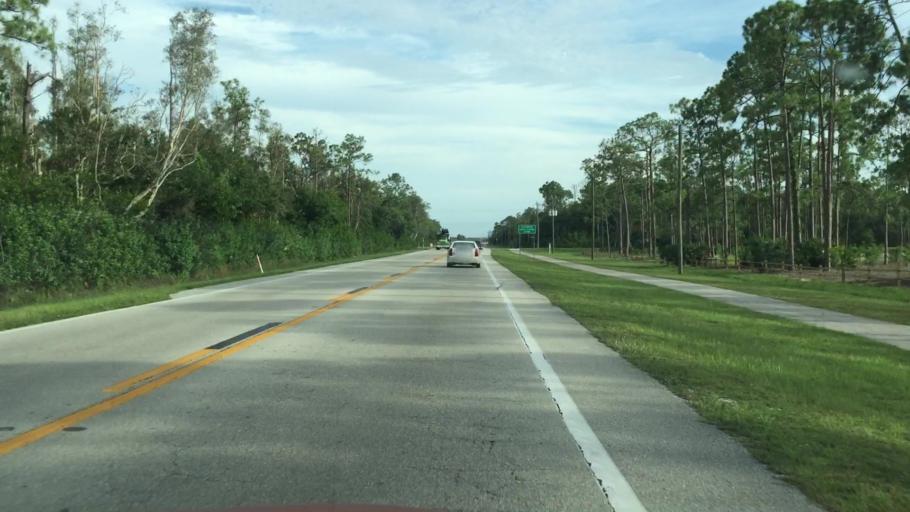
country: US
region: Florida
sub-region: Lee County
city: Fort Myers
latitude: 26.6220
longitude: -81.8116
